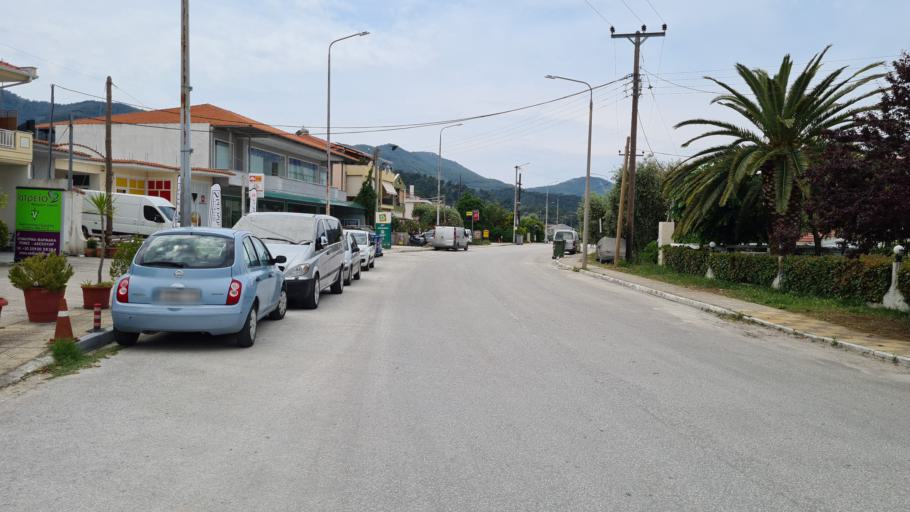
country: GR
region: East Macedonia and Thrace
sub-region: Nomos Kavalas
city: Thasos
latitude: 40.7754
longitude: 24.7029
